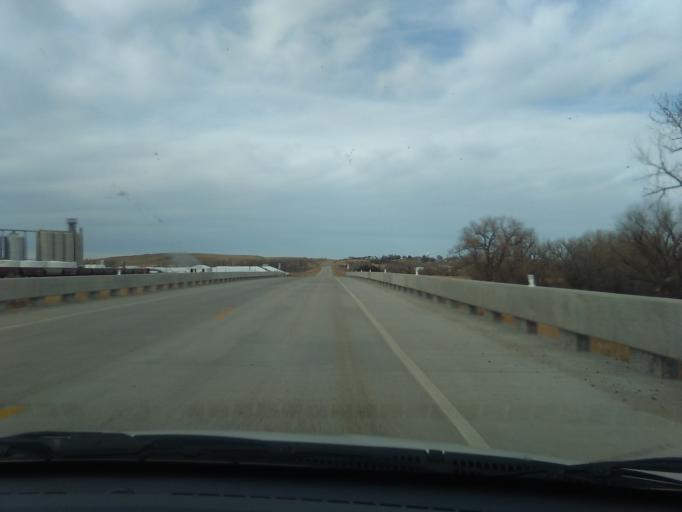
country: US
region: Nebraska
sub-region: Dundy County
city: Benkelman
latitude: 40.0338
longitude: -101.5431
